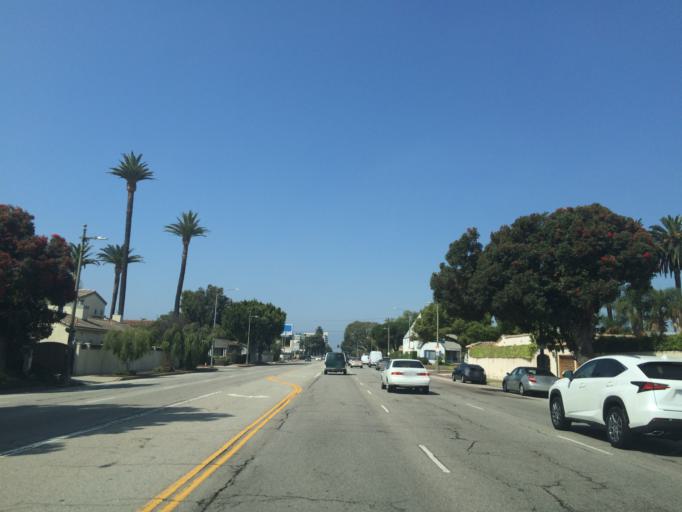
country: US
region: California
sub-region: Los Angeles County
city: Westwood, Los Angeles
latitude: 34.0454
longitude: -118.4292
